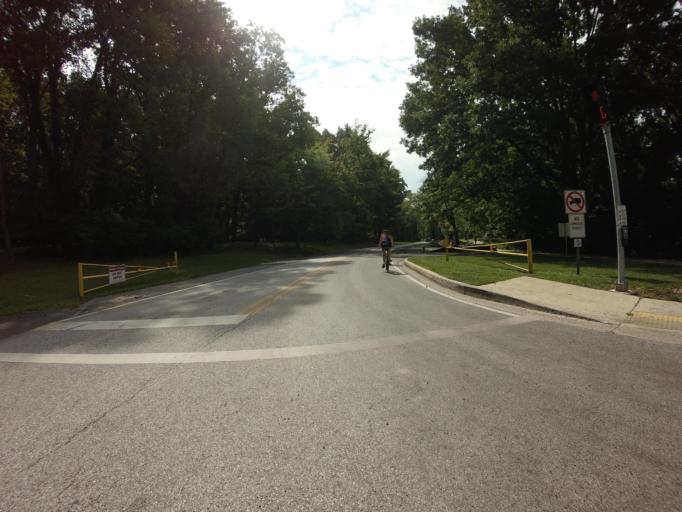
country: US
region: Maryland
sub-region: Montgomery County
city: South Kensington
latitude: 39.0123
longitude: -77.0908
